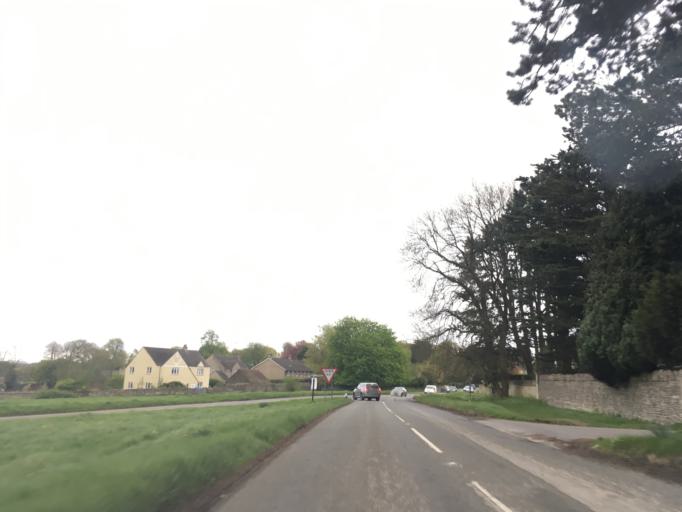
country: GB
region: England
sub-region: Gloucestershire
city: Brimscombe
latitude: 51.7249
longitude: -2.2136
